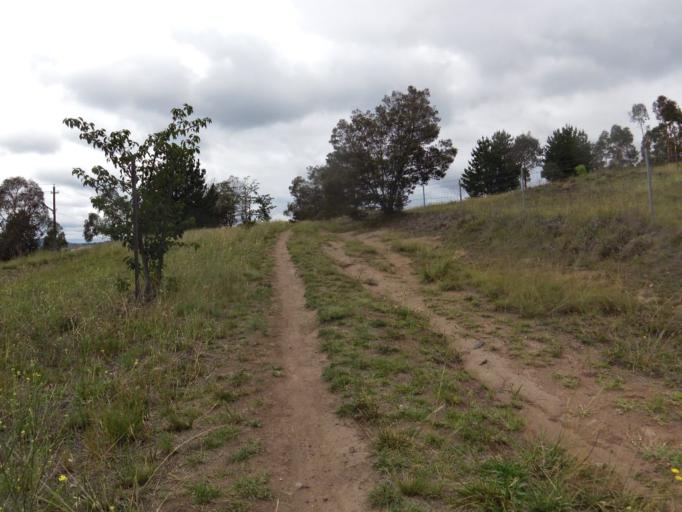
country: AU
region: Australian Capital Territory
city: Macquarie
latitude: -35.3387
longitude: 149.0270
